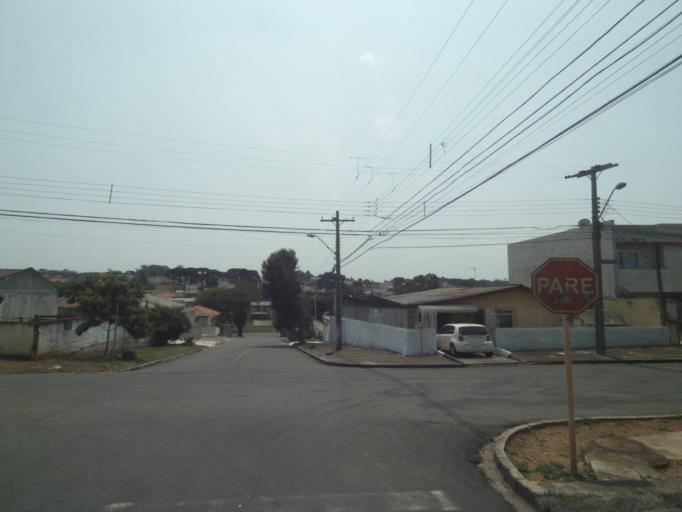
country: BR
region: Parana
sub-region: Sao Jose Dos Pinhais
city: Sao Jose dos Pinhais
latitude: -25.5263
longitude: -49.2495
